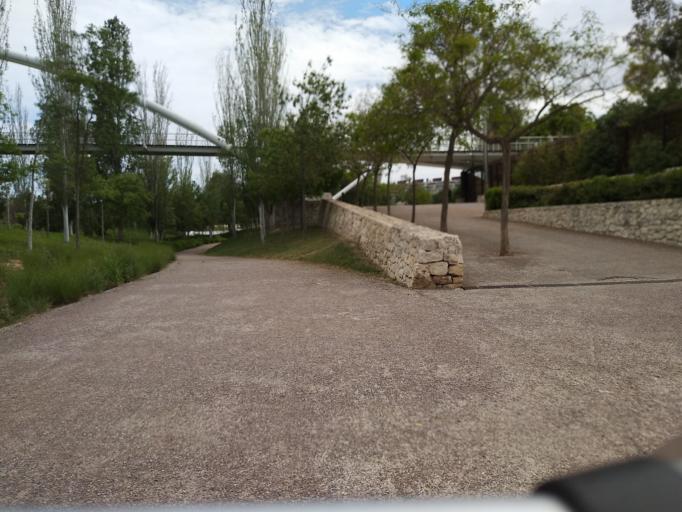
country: ES
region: Valencia
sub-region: Provincia de Valencia
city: Mislata
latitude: 39.4783
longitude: -0.4096
